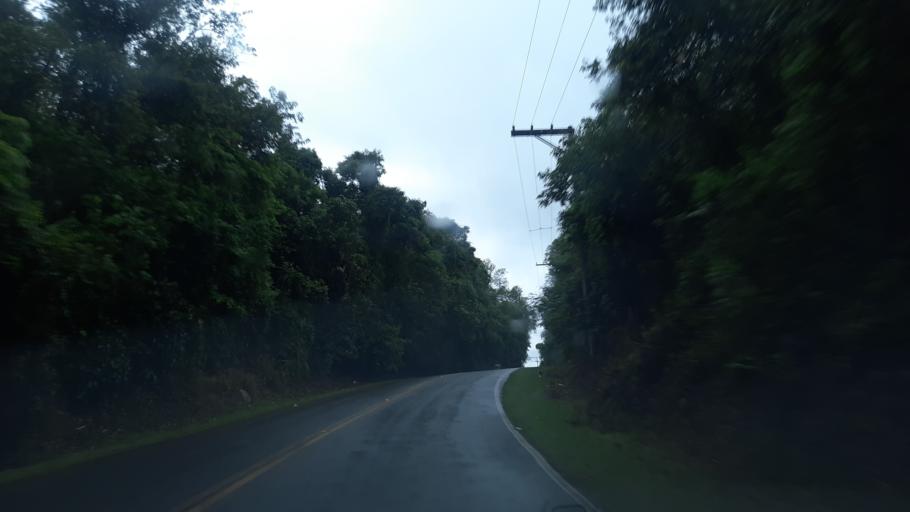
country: BR
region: Sao Paulo
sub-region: Atibaia
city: Atibaia
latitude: -23.0905
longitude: -46.5390
